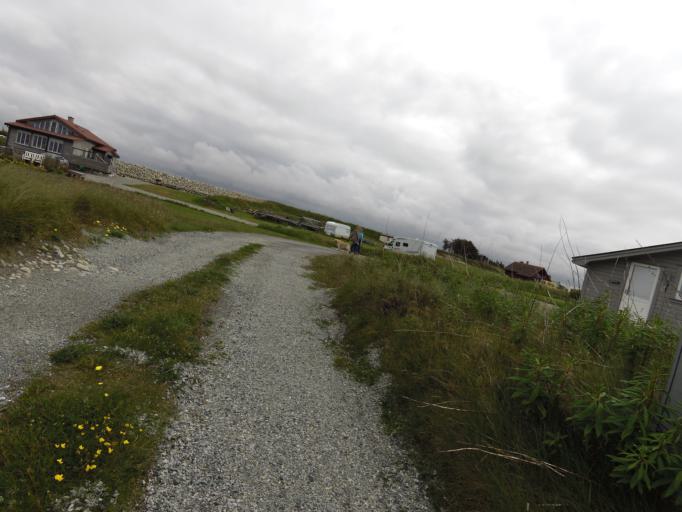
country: NO
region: Rogaland
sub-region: Klepp
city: Kleppe
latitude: 58.8144
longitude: 5.5485
